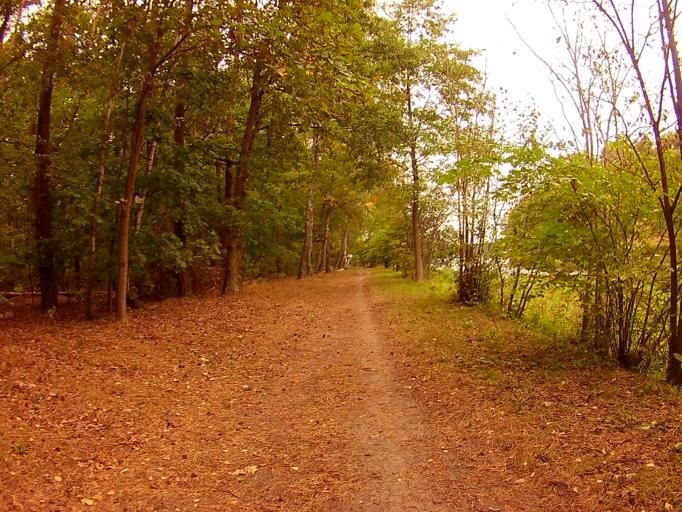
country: DE
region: Berlin
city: Schmockwitz
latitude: 52.3776
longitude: 13.6781
